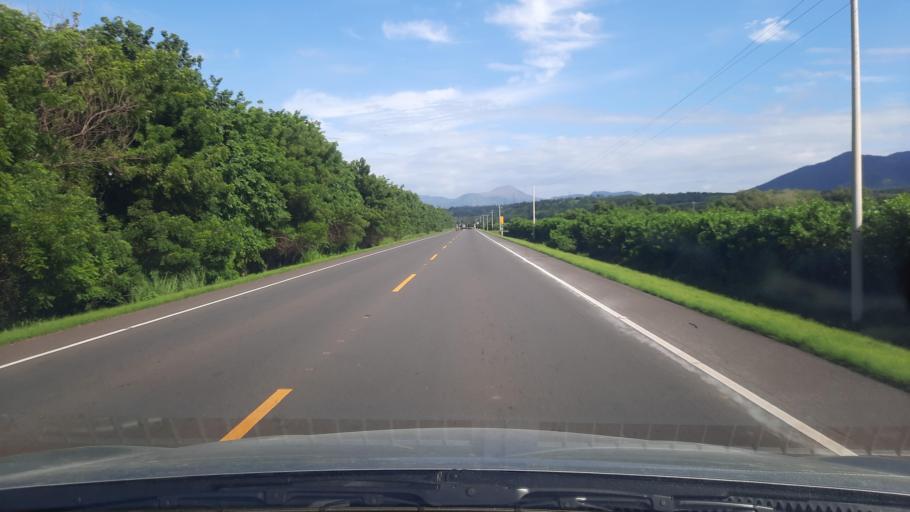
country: NI
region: Chinandega
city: Chichigalpa
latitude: 12.7499
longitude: -86.8954
